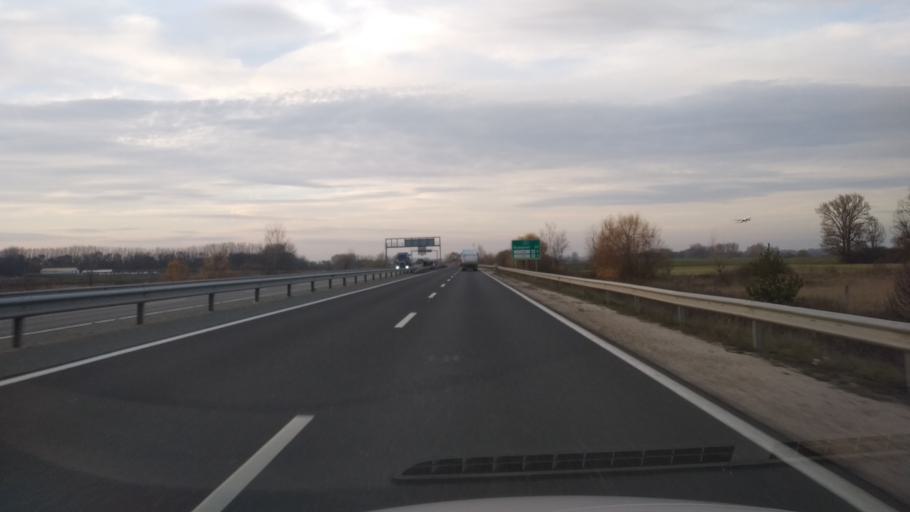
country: HU
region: Pest
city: Vecses
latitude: 47.4093
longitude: 19.2972
